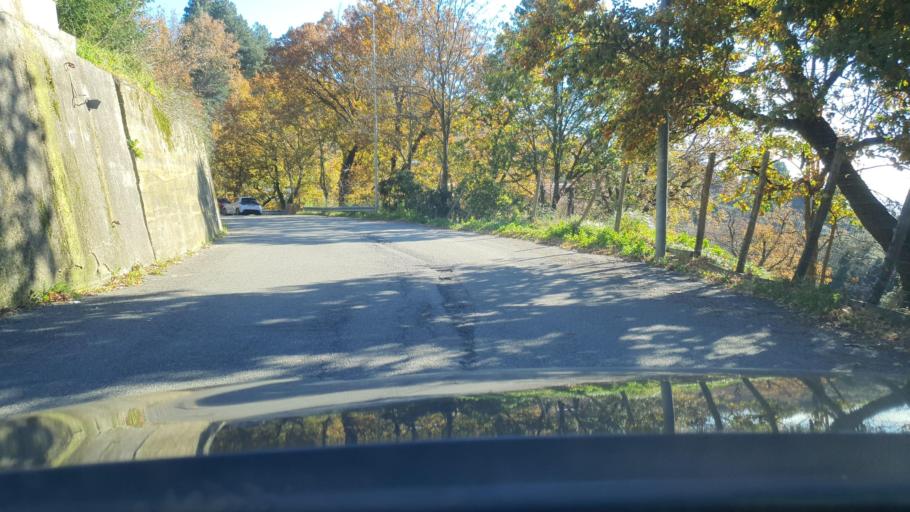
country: IT
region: Calabria
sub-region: Provincia di Catanzaro
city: Sant'Elia
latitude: 38.9636
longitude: 16.5788
